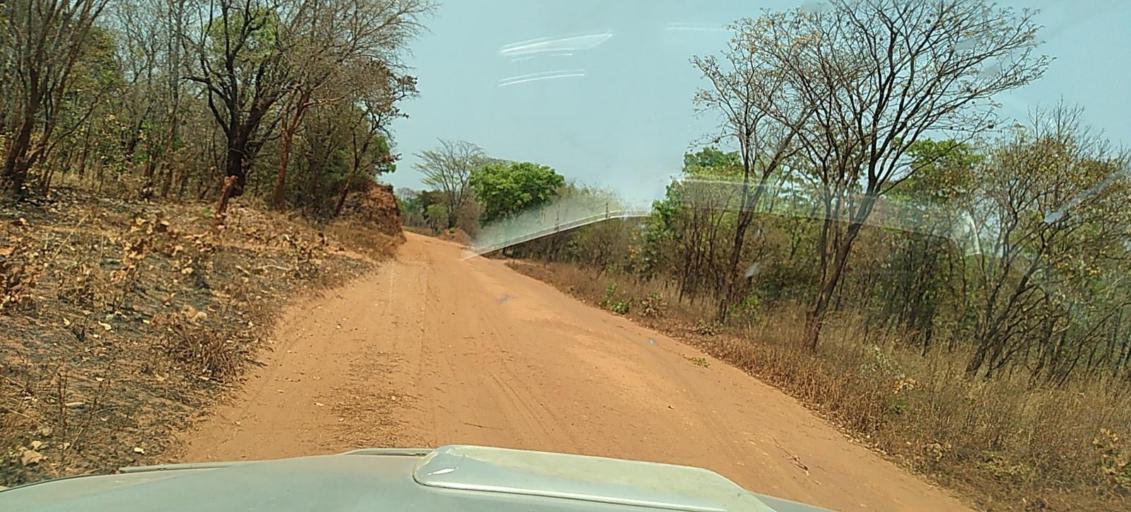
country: ZM
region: North-Western
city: Kasempa
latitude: -13.6243
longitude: 26.2112
